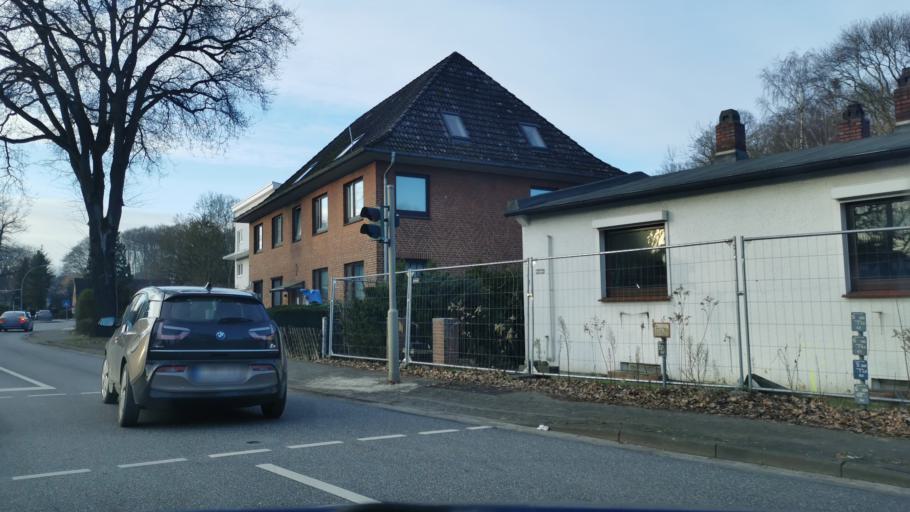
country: DE
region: Hamburg
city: Harburg
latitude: 53.4359
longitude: 9.9686
